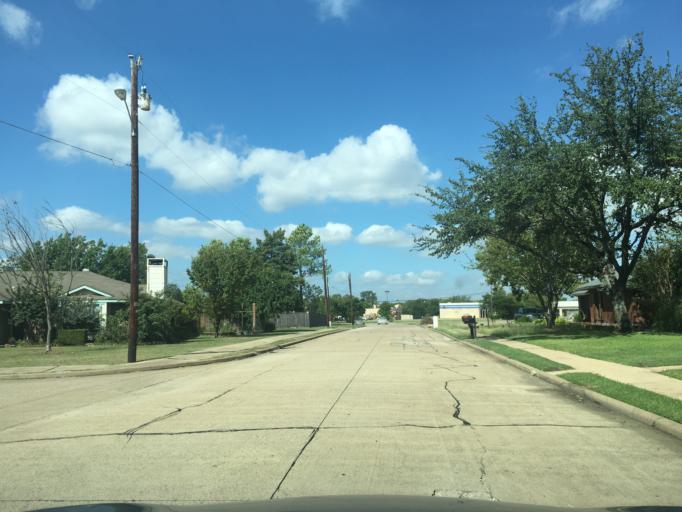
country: US
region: Texas
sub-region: Dallas County
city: Sachse
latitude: 32.9700
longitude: -96.5997
